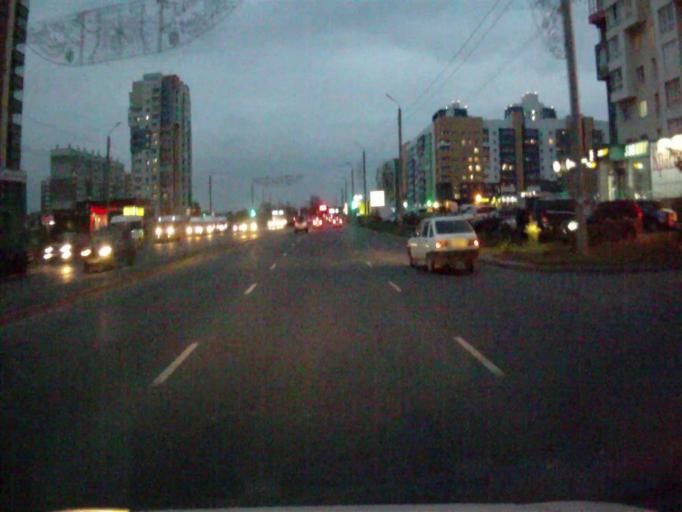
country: RU
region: Chelyabinsk
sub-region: Gorod Chelyabinsk
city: Chelyabinsk
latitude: 55.1645
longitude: 61.2949
